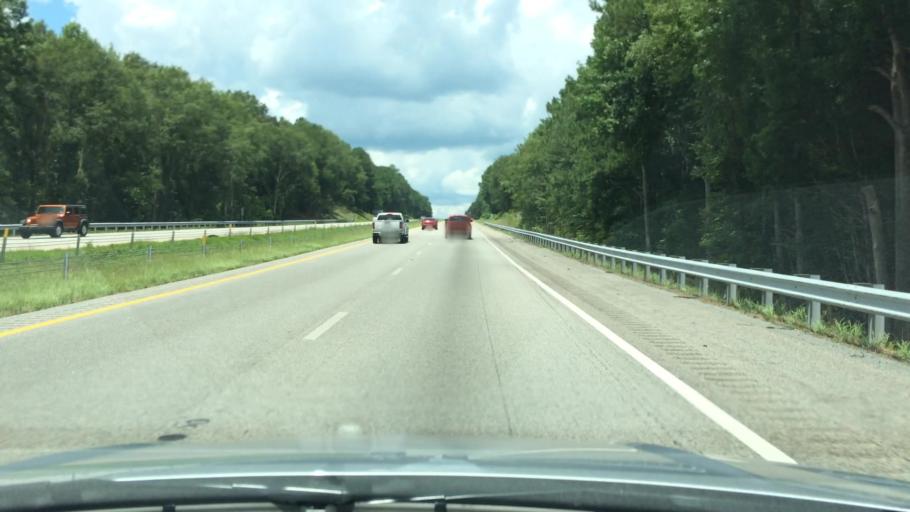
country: US
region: South Carolina
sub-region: Laurens County
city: Watts Mills
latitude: 34.6050
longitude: -81.8929
